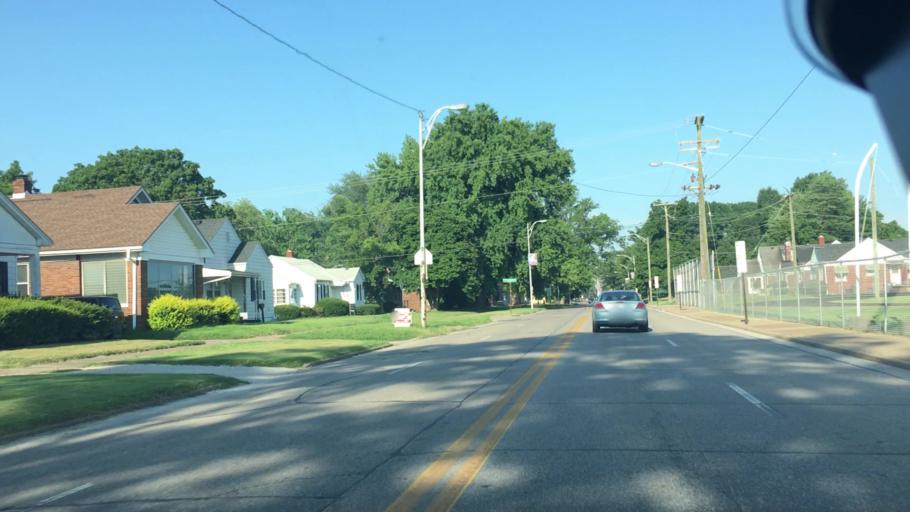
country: US
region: Indiana
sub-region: Vanderburgh County
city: Evansville
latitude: 37.9736
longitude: -87.5369
